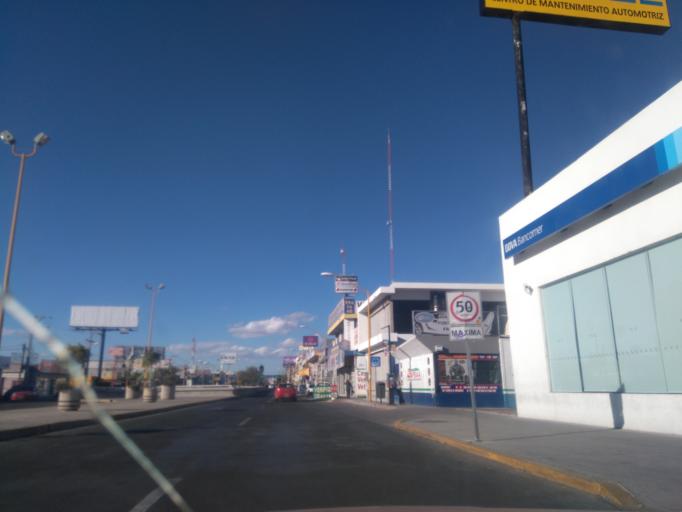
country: MX
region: Aguascalientes
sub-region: Aguascalientes
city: Aguascalientes
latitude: 21.8745
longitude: -102.3119
